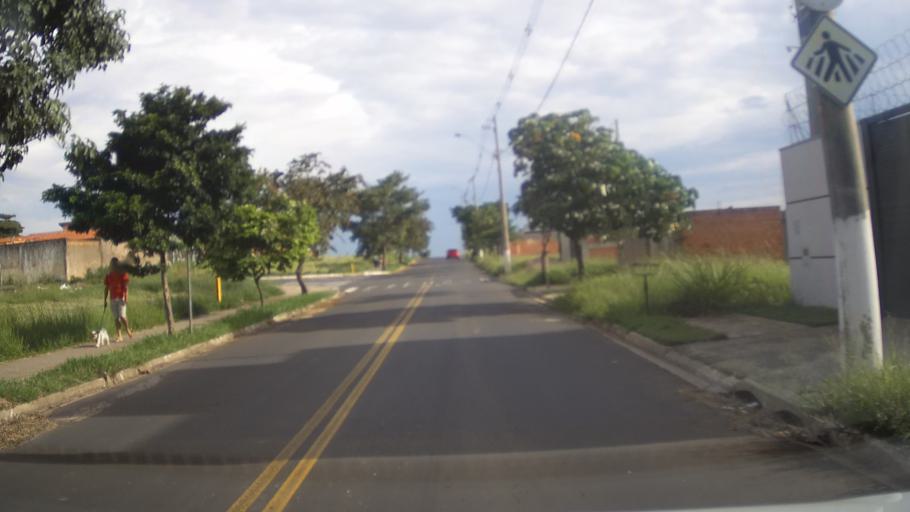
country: BR
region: Sao Paulo
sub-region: Campinas
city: Campinas
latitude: -22.9178
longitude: -47.1161
